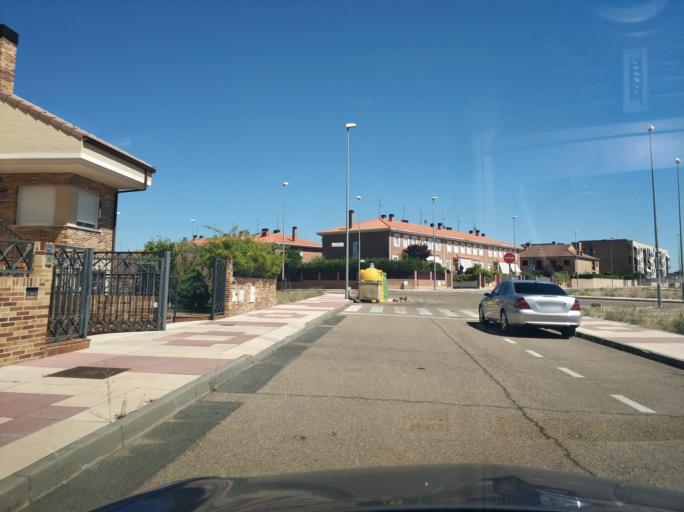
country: ES
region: Castille and Leon
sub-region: Provincia de Salamanca
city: Carbajosa de la Sagrada
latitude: 40.9368
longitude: -5.6476
